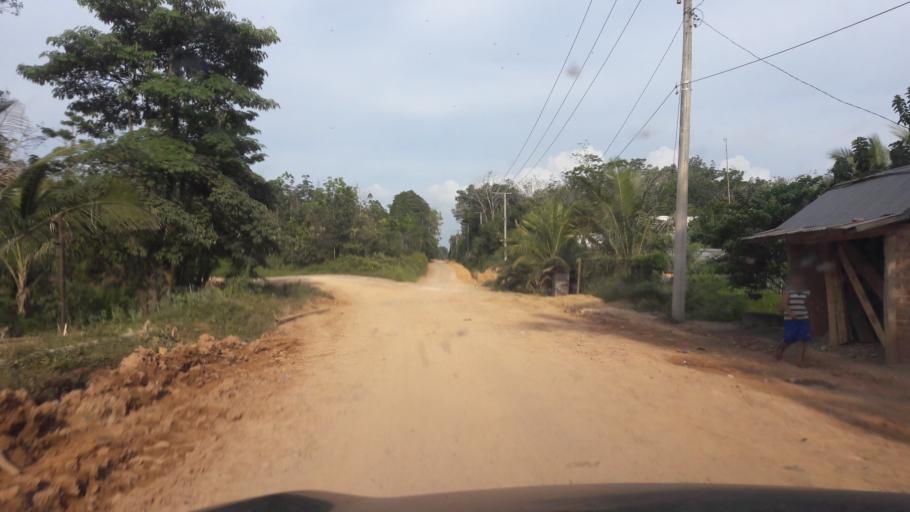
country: ID
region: South Sumatra
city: Gunungmenang
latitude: -3.2656
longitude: 104.0406
